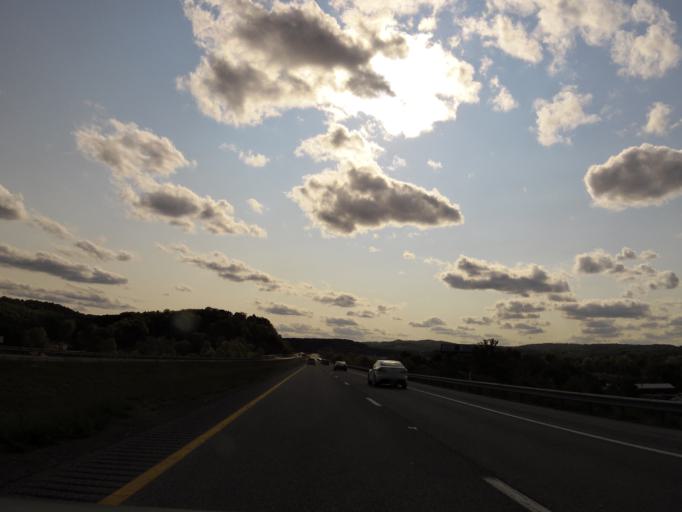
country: US
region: West Virginia
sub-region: Mercer County
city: Princeton
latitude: 37.3606
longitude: -81.0817
